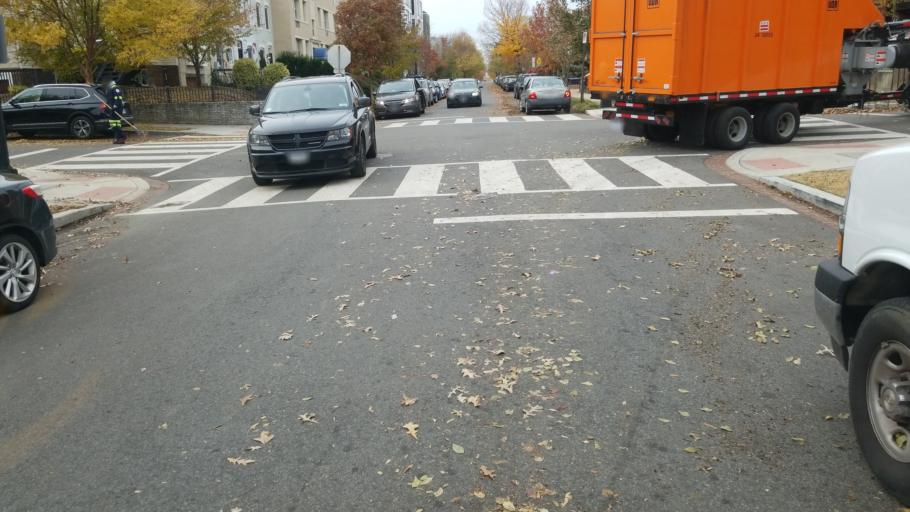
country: US
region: Maryland
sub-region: Prince George's County
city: Hillcrest Heights
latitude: 38.8784
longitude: -76.9853
